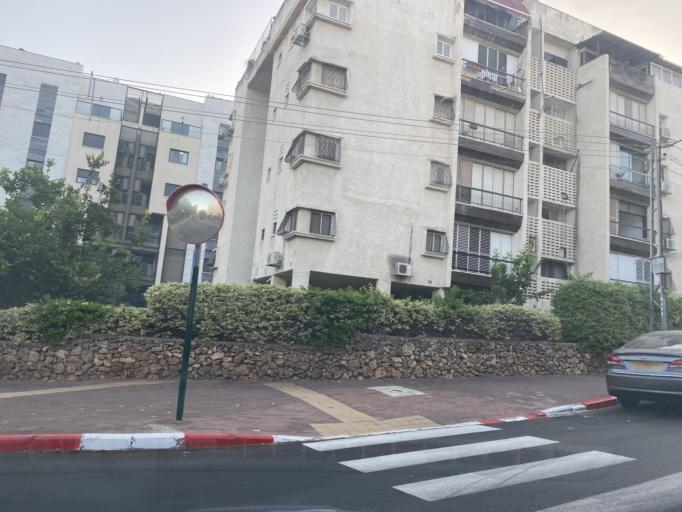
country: IL
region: Central District
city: Hod HaSharon
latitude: 32.1579
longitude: 34.9019
